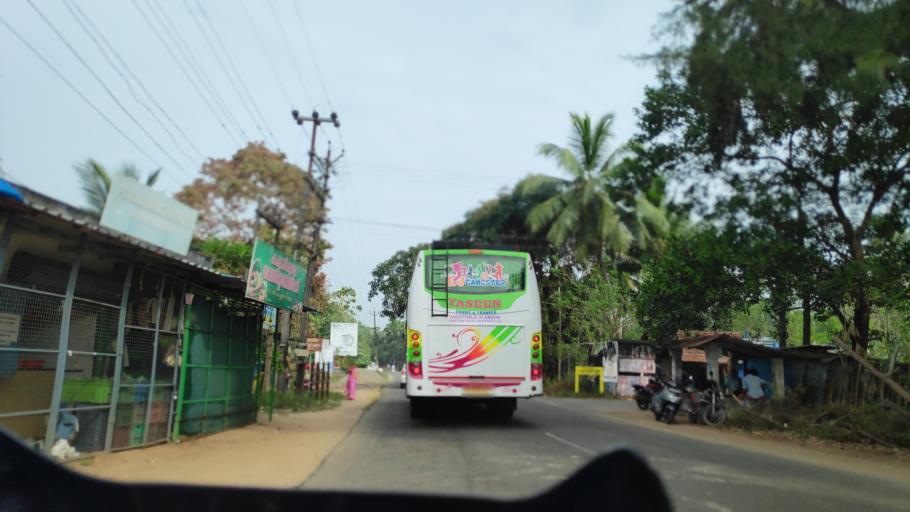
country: IN
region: Kerala
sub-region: Alappuzha
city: Kutiatodu
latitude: 9.8186
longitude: 76.3509
